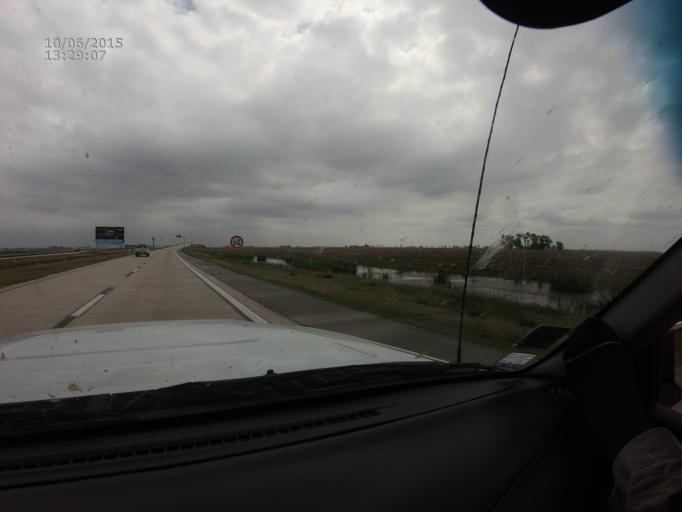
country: AR
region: Cordoba
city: Leones
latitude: -32.6396
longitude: -62.2378
